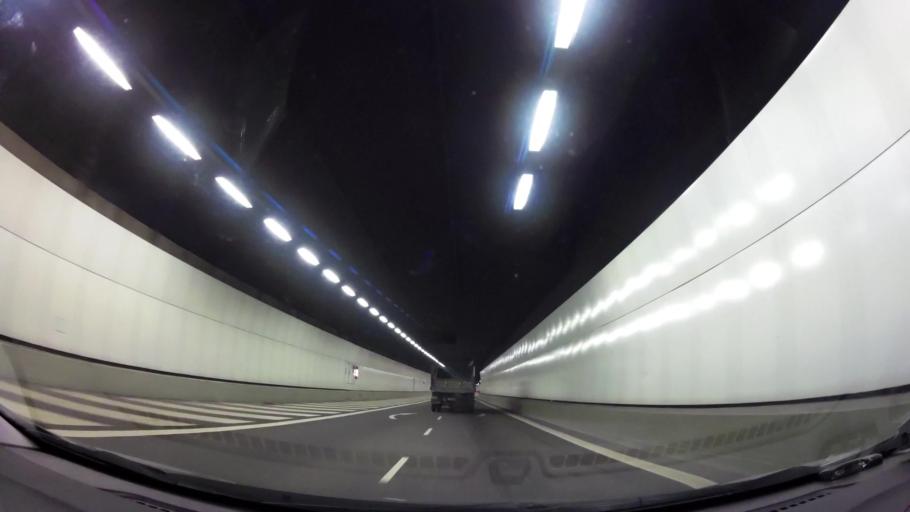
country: SG
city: Singapore
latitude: 1.3279
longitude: 103.8811
